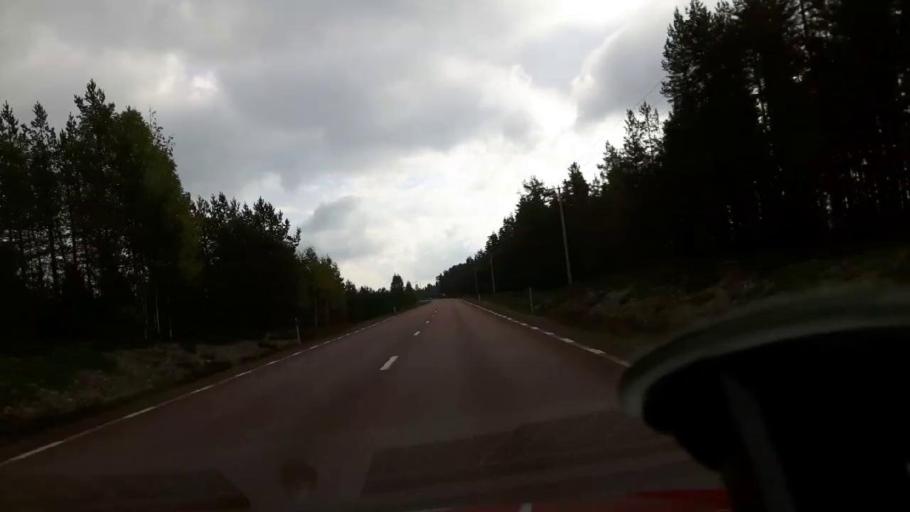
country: SE
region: Gaevleborg
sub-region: Soderhamns Kommun
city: Ljusne
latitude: 61.1025
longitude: 16.9460
